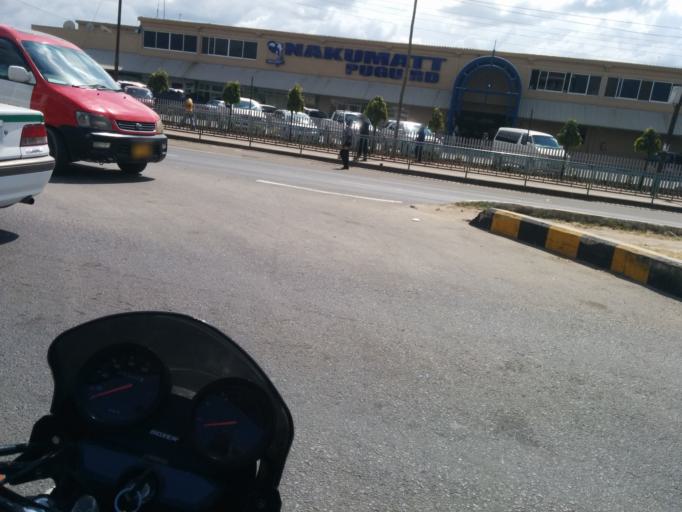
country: TZ
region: Dar es Salaam
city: Dar es Salaam
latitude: -6.8283
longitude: 39.2752
